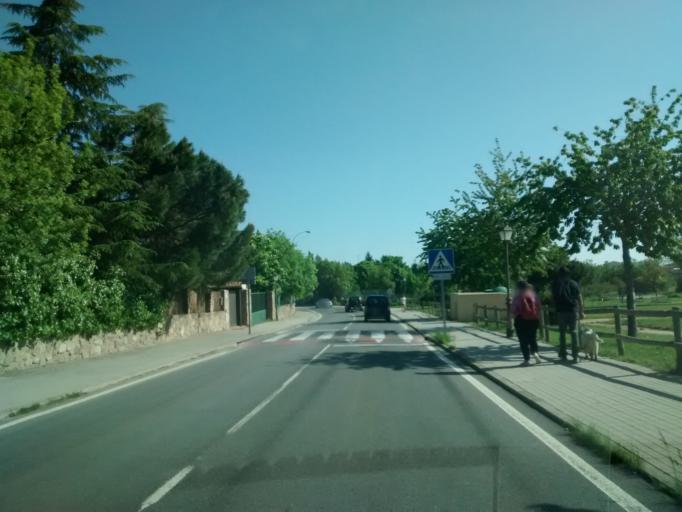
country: ES
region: Castille and Leon
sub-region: Provincia de Segovia
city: Torrecaballeros
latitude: 40.9928
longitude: -4.0224
